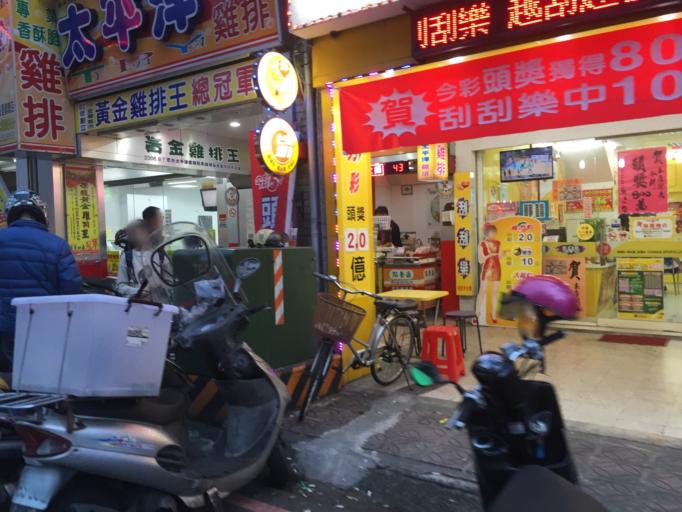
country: TW
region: Taiwan
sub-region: Yilan
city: Yilan
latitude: 24.7603
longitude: 121.7532
